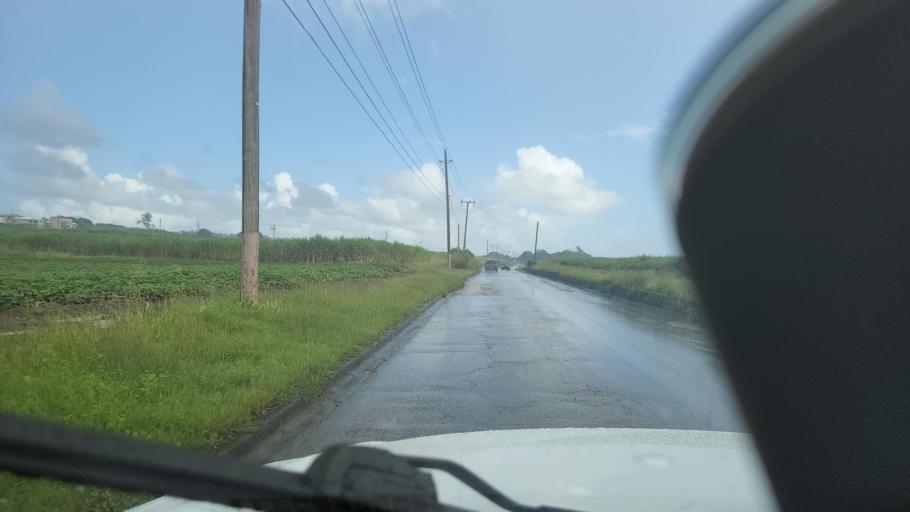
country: BB
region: Saint Michael
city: Bridgetown
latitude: 13.1222
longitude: -59.5650
